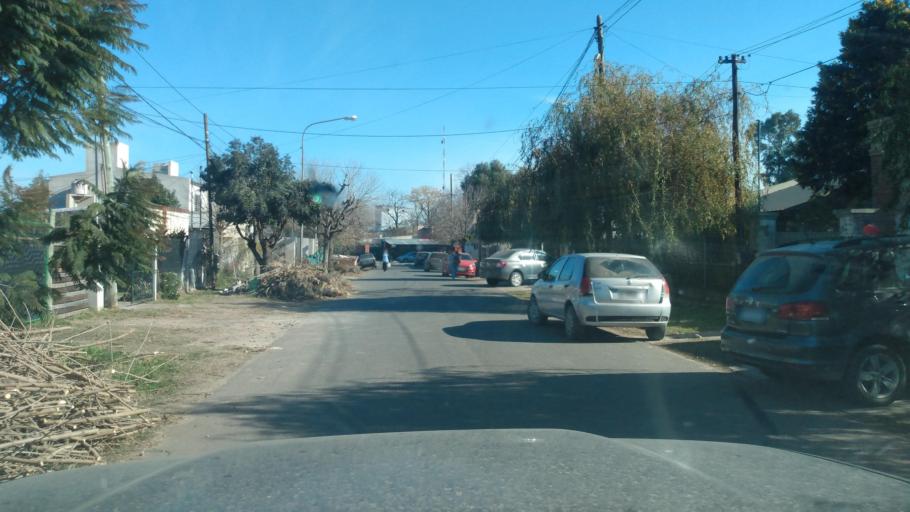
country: AR
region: Buenos Aires
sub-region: Partido de Lujan
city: Lujan
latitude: -34.5848
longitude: -59.1109
